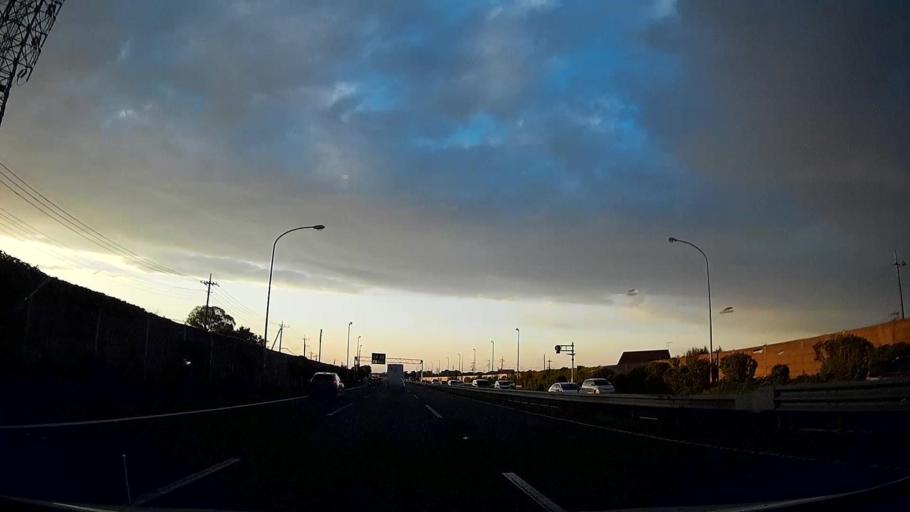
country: JP
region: Saitama
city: Kukichuo
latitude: 36.0557
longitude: 139.6558
